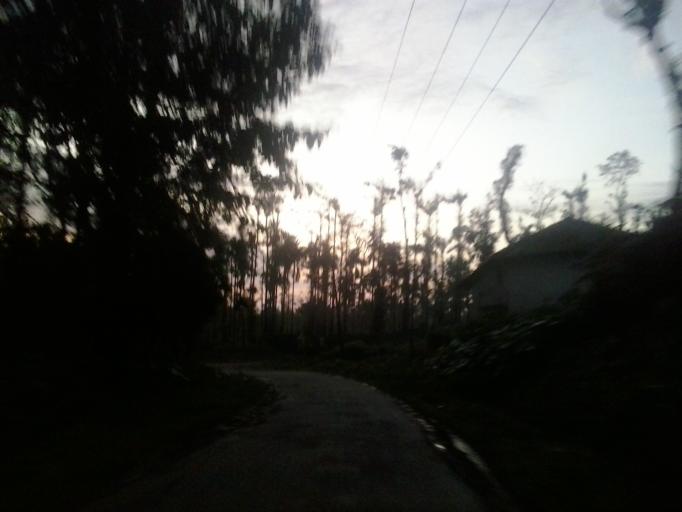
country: IN
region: Karnataka
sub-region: Hassan
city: Sakleshpur
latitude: 13.0023
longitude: 75.6875
